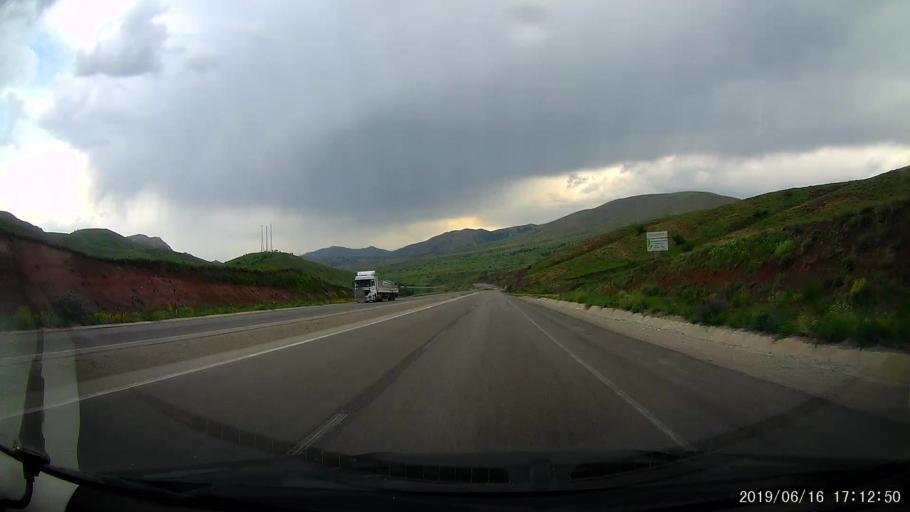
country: TR
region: Erzurum
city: Askale
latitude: 39.8594
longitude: 40.6118
